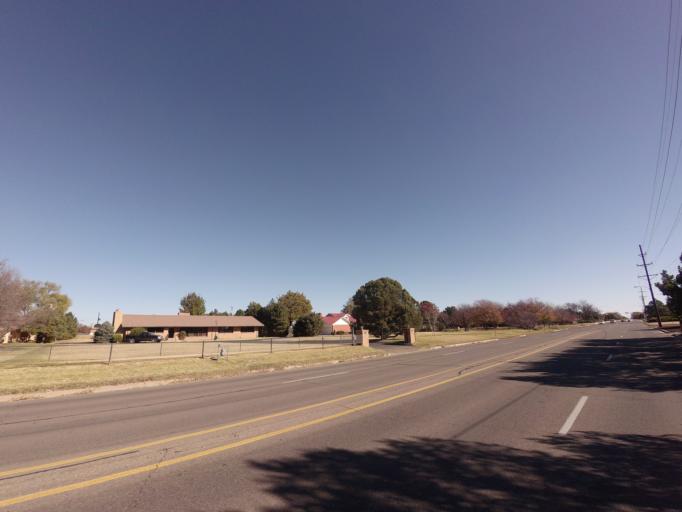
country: US
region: New Mexico
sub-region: Curry County
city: Clovis
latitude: 34.4193
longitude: -103.1820
